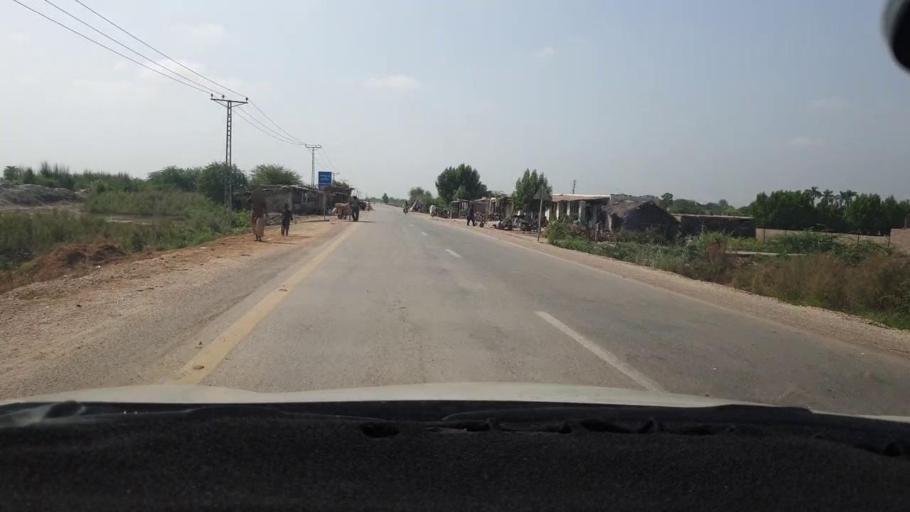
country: PK
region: Sindh
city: Mirpur Khas
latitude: 25.7549
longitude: 69.0847
